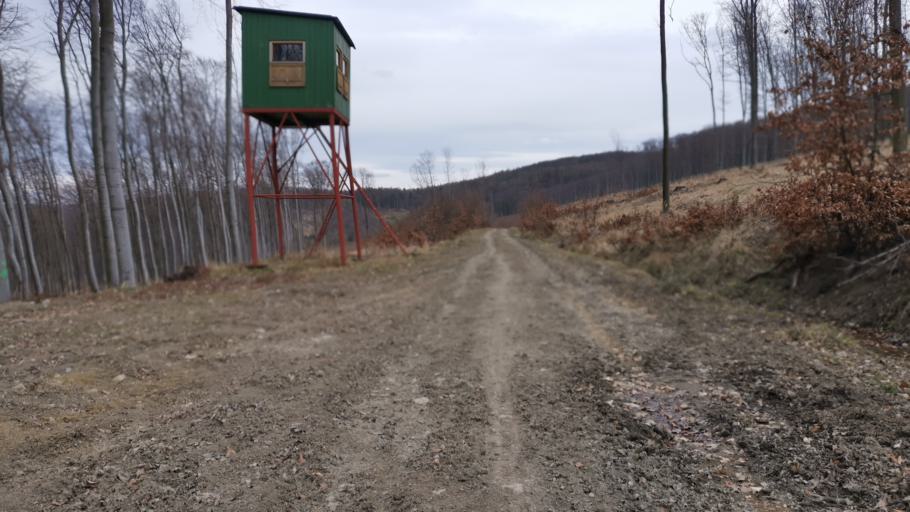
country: CZ
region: South Moravian
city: Knezdub
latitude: 48.8190
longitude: 17.3465
